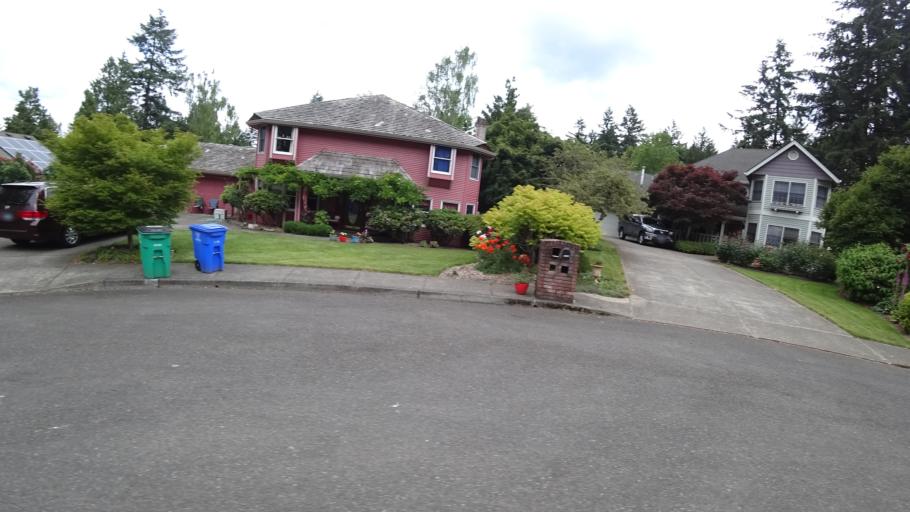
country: US
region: Oregon
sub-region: Clackamas County
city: Lake Oswego
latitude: 45.4505
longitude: -122.7070
